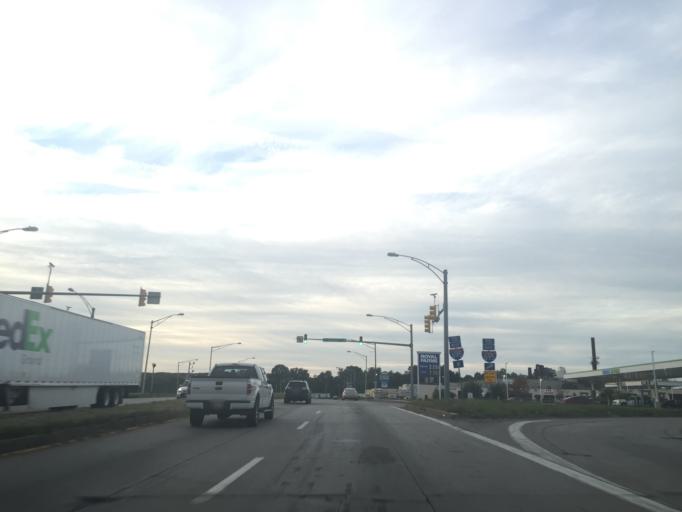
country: US
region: Maryland
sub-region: Anne Arundel County
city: Riviera Beach
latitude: 39.1995
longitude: -76.5556
